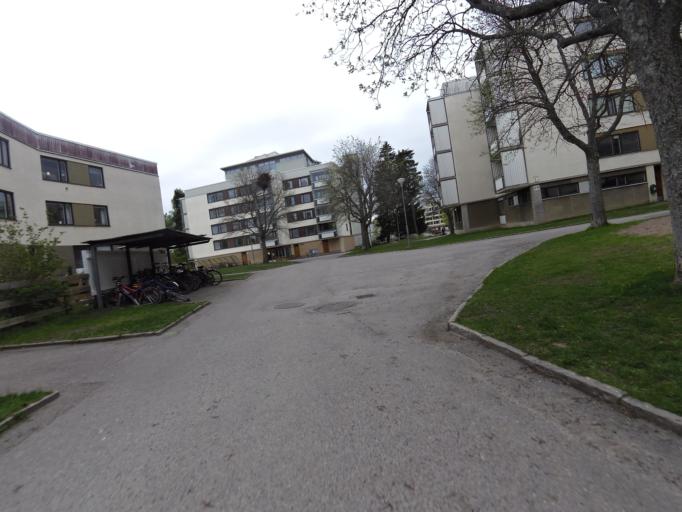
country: SE
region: Gaevleborg
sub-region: Gavle Kommun
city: Gavle
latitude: 60.6910
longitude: 17.1204
